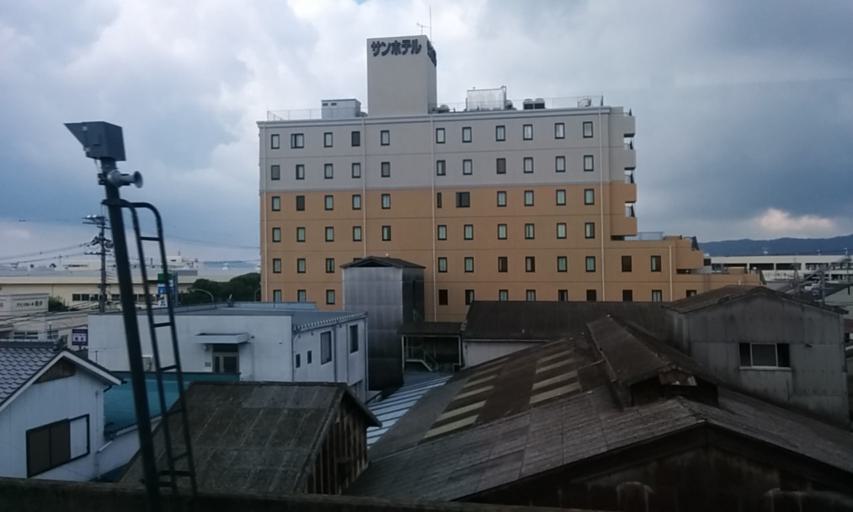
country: JP
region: Nara
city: Tenri
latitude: 34.6197
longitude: 135.7807
